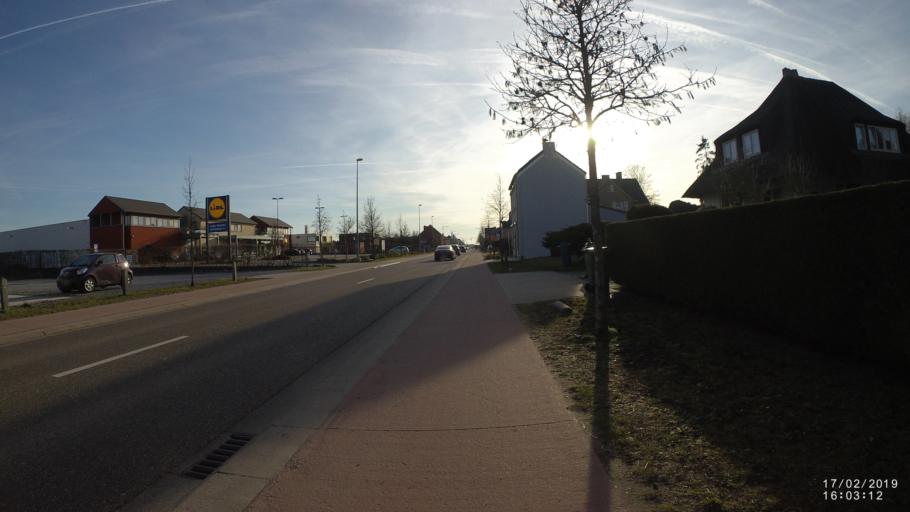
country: BE
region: Flanders
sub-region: Provincie Limburg
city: Alken
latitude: 50.9046
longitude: 5.3138
